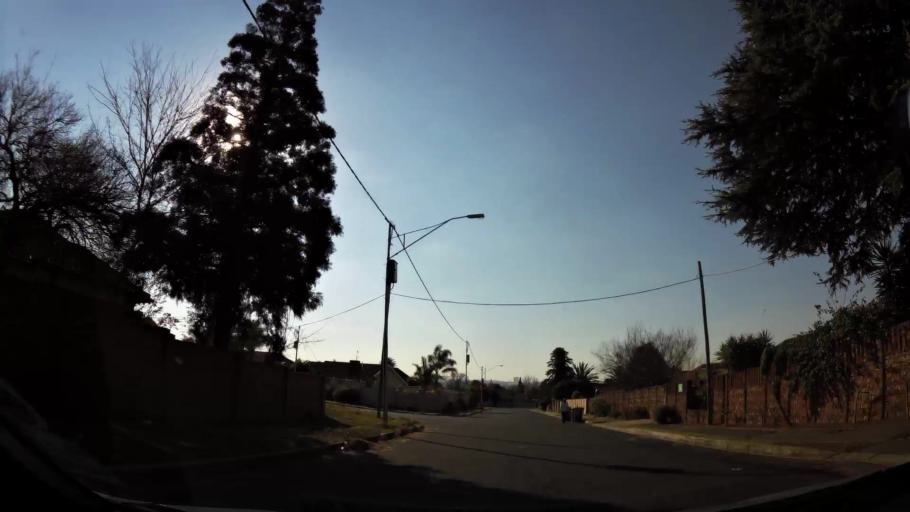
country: ZA
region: Gauteng
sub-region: City of Johannesburg Metropolitan Municipality
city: Johannesburg
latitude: -26.2463
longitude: 28.0119
